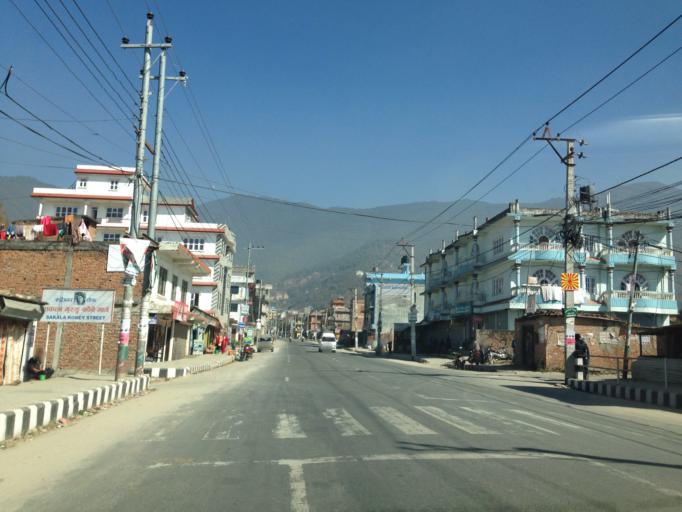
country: NP
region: Central Region
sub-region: Bagmati Zone
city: Kathmandu
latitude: 27.7713
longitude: 85.3586
